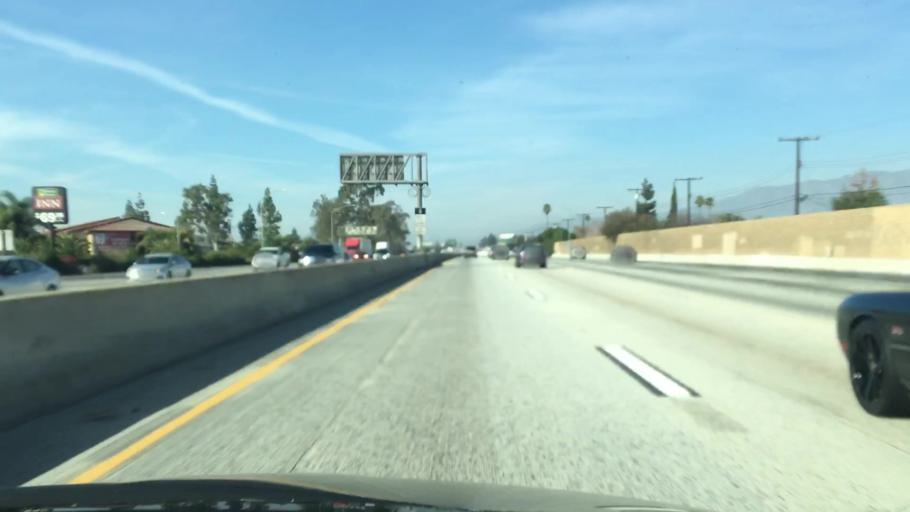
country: US
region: California
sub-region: San Bernardino County
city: Ontario
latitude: 34.0715
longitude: -117.6125
